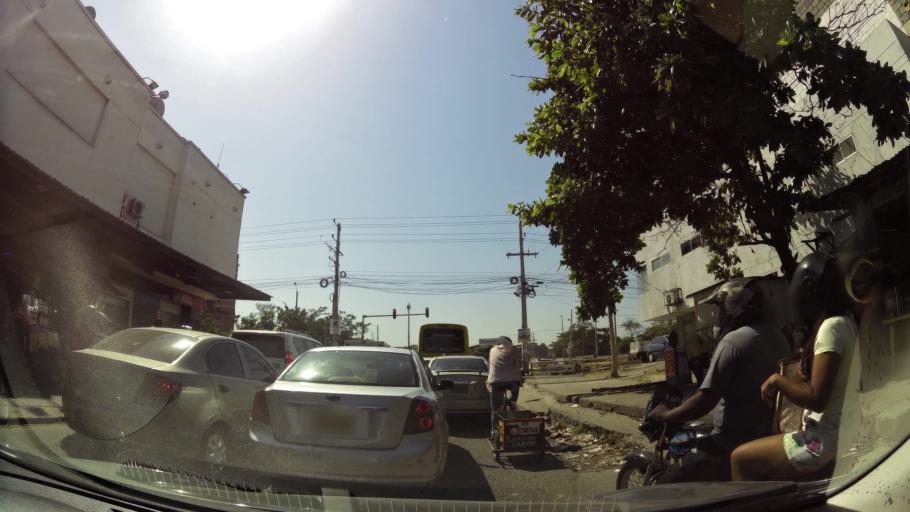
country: CO
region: Bolivar
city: Cartagena
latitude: 10.3888
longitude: -75.5032
